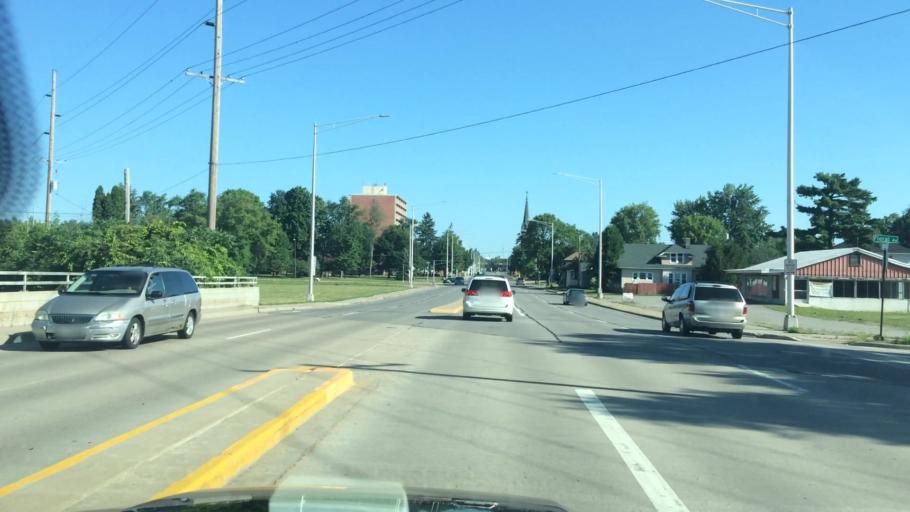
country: US
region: Wisconsin
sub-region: Marathon County
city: Wausau
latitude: 44.9496
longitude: -89.6220
